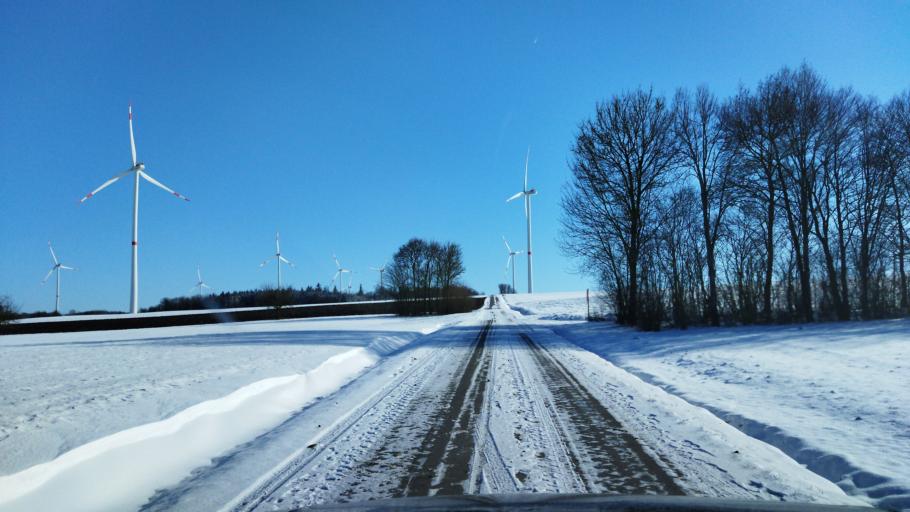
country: DE
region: Baden-Wuerttemberg
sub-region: Regierungsbezirk Stuttgart
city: Ilshofen
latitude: 49.1926
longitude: 9.9402
